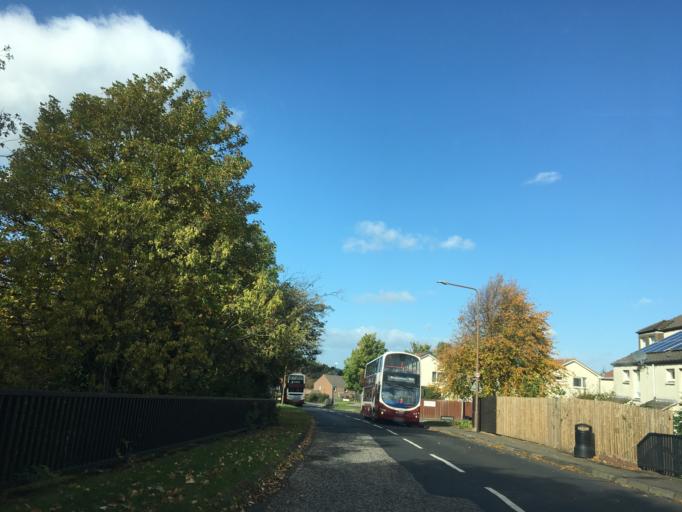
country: GB
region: Scotland
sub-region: Edinburgh
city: Currie
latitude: 55.9533
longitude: -3.3057
